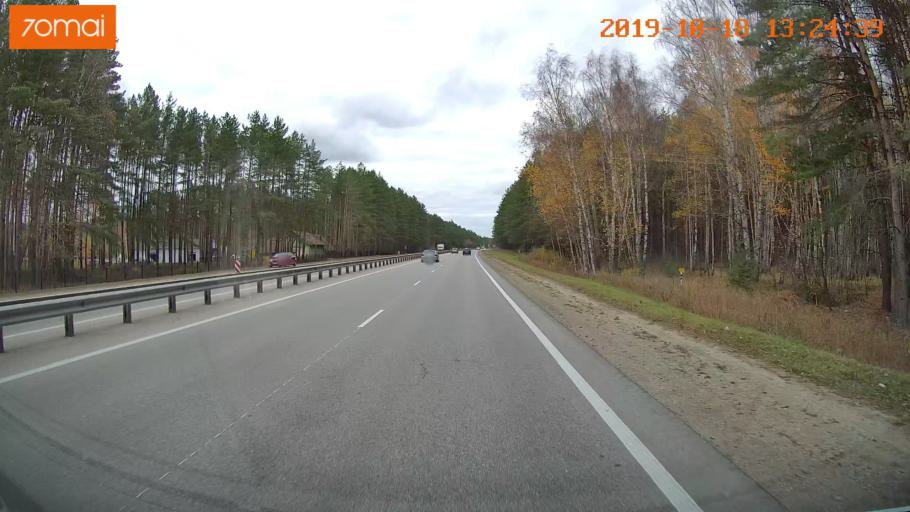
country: RU
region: Rjazan
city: Polyany
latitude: 54.7337
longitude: 39.8426
